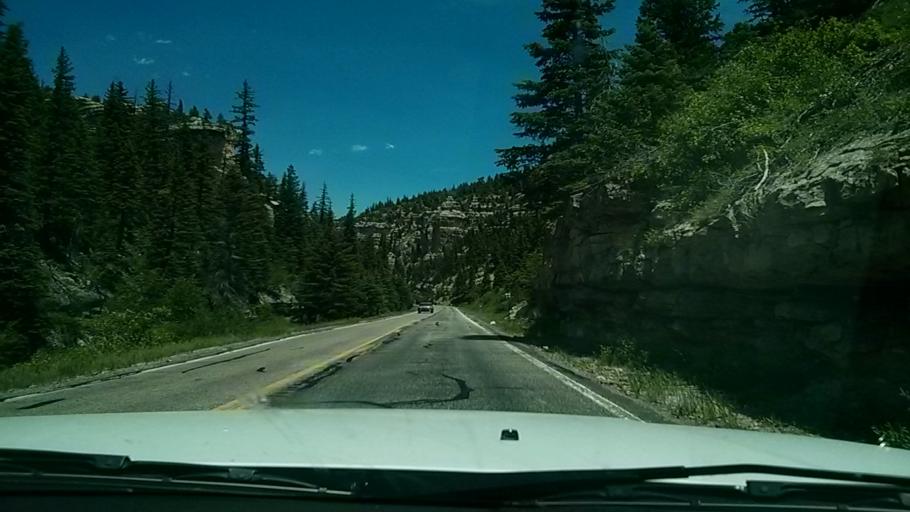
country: US
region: Utah
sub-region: Iron County
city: Cedar City
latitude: 37.6132
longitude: -112.9326
